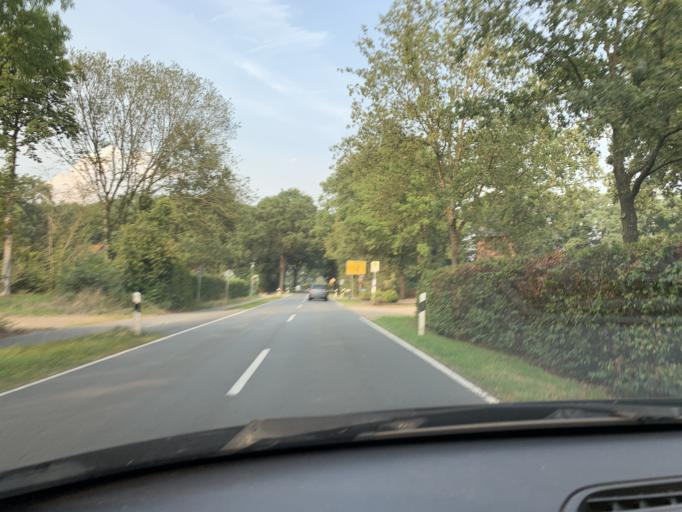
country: DE
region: Lower Saxony
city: Apen
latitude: 53.1773
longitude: 7.7776
